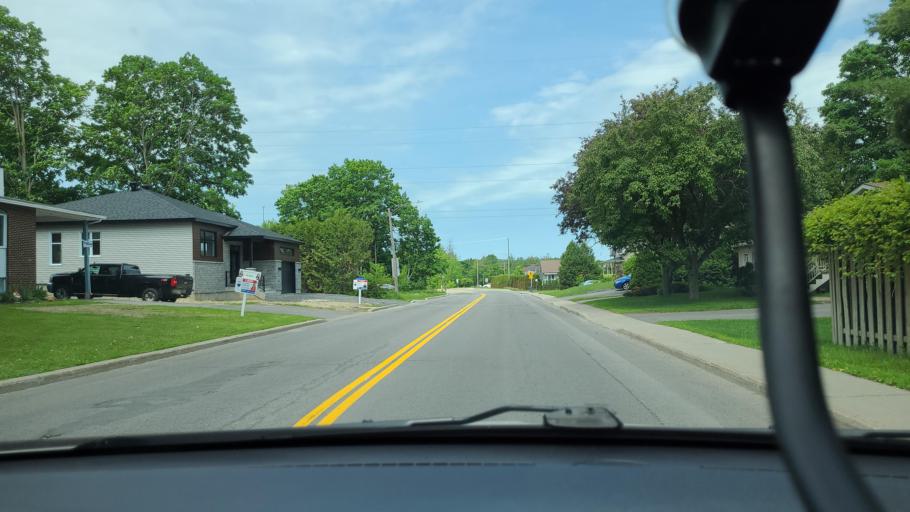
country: CA
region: Quebec
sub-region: Lanaudiere
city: Crabtree
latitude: 45.9692
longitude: -73.4806
